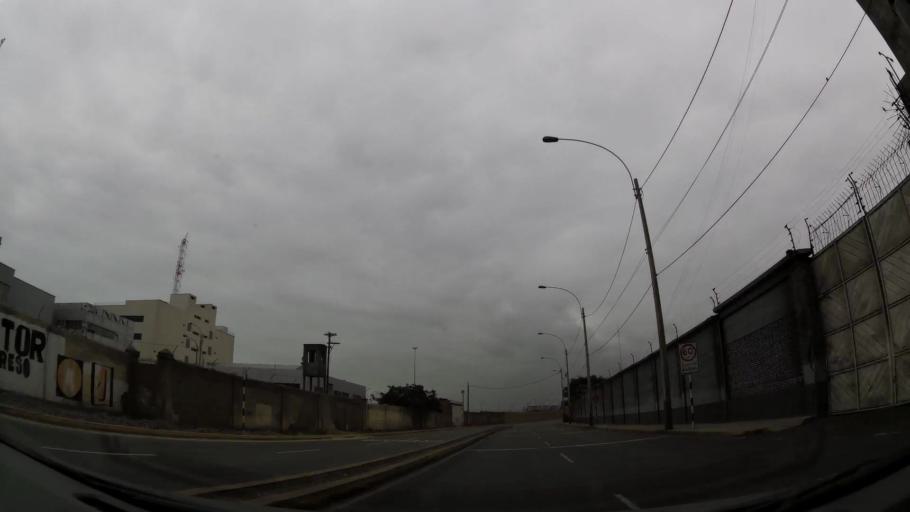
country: PE
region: Callao
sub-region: Callao
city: Callao
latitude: -12.0509
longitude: -77.1404
